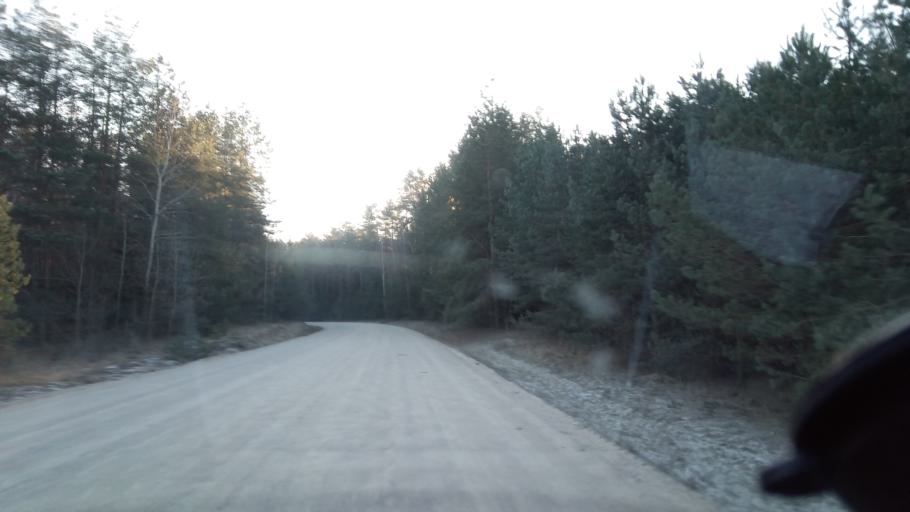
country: LT
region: Alytaus apskritis
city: Druskininkai
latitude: 54.1477
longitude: 23.9375
